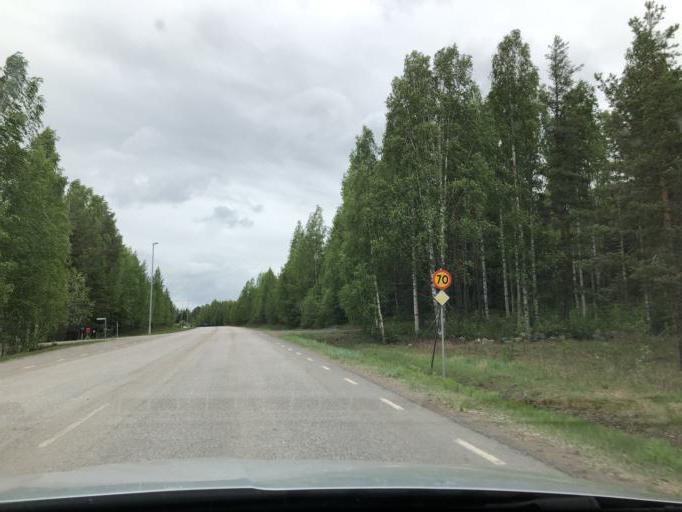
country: SE
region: Norrbotten
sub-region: Pitea Kommun
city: Bergsviken
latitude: 65.3813
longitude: 21.3385
